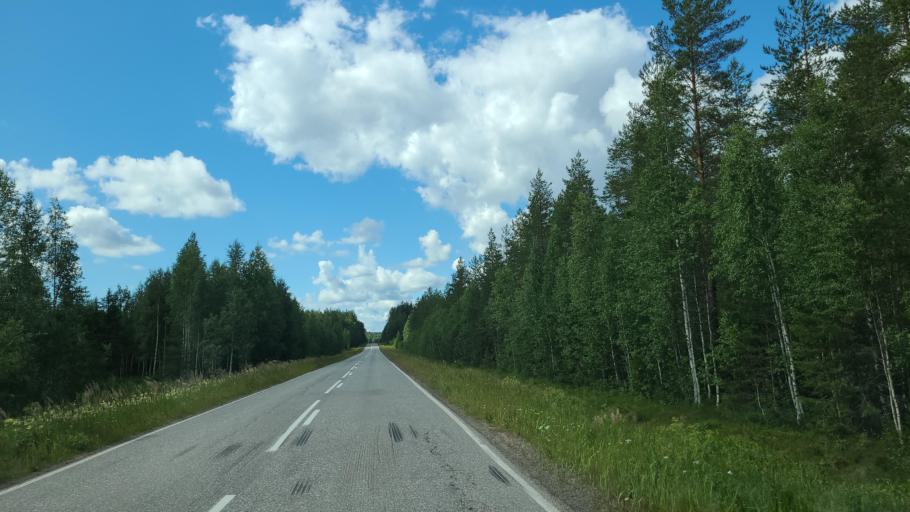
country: FI
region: Northern Savo
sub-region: Koillis-Savo
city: Kaavi
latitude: 62.9809
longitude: 28.8013
